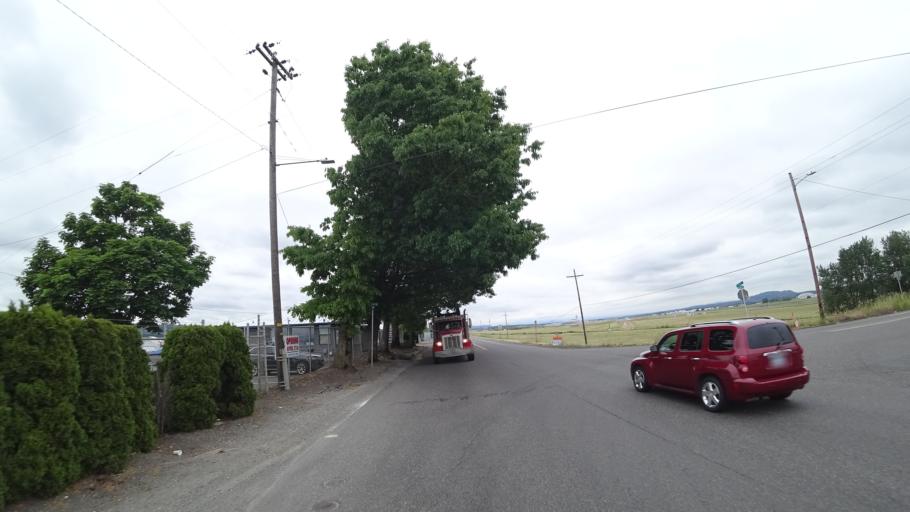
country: US
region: Washington
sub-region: Clark County
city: Vancouver
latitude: 45.6005
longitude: -122.6355
